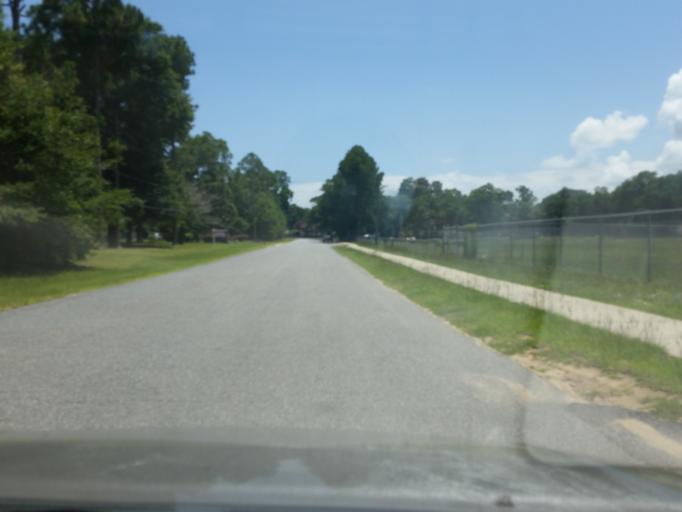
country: US
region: Florida
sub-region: Escambia County
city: Ferry Pass
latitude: 30.5123
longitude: -87.1970
